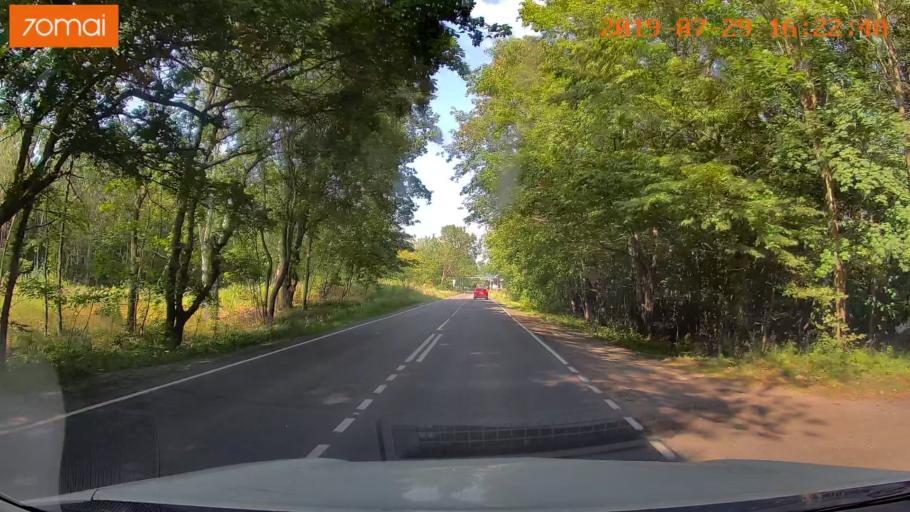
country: RU
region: Kaliningrad
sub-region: Gorod Kaliningrad
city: Baltiysk
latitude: 54.7011
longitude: 19.9417
